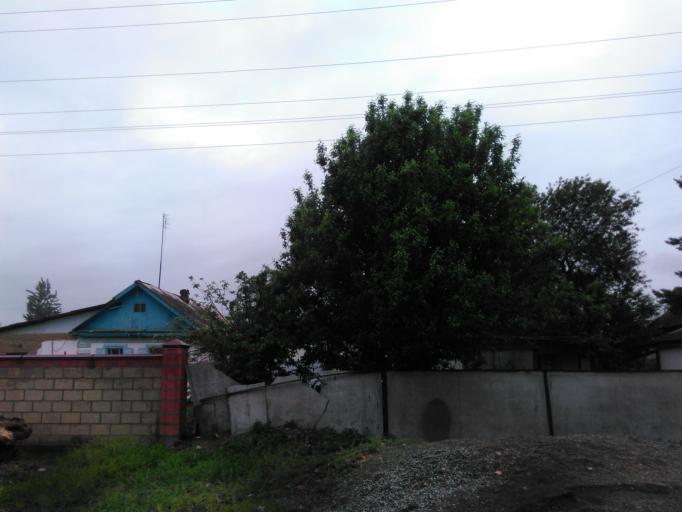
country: KG
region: Chuy
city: Tokmok
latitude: 42.8150
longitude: 75.3219
